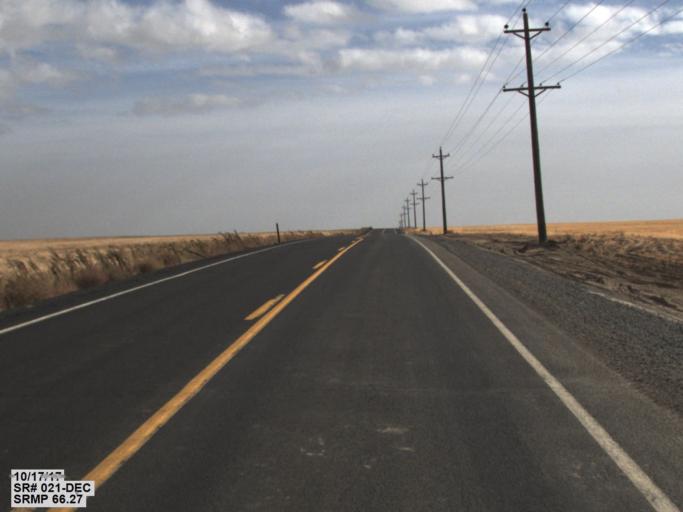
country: US
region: Washington
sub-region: Adams County
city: Ritzville
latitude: 47.4551
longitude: -118.7504
